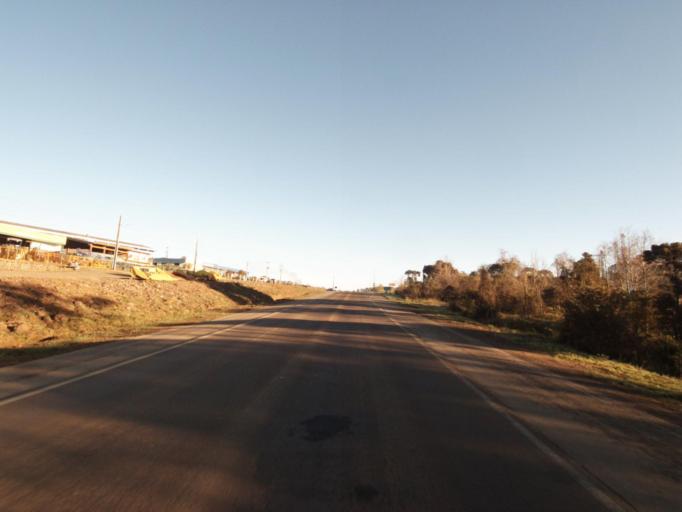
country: BR
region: Santa Catarina
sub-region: Sao Lourenco Do Oeste
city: Sao Lourenco dOeste
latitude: -26.7758
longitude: -53.2020
